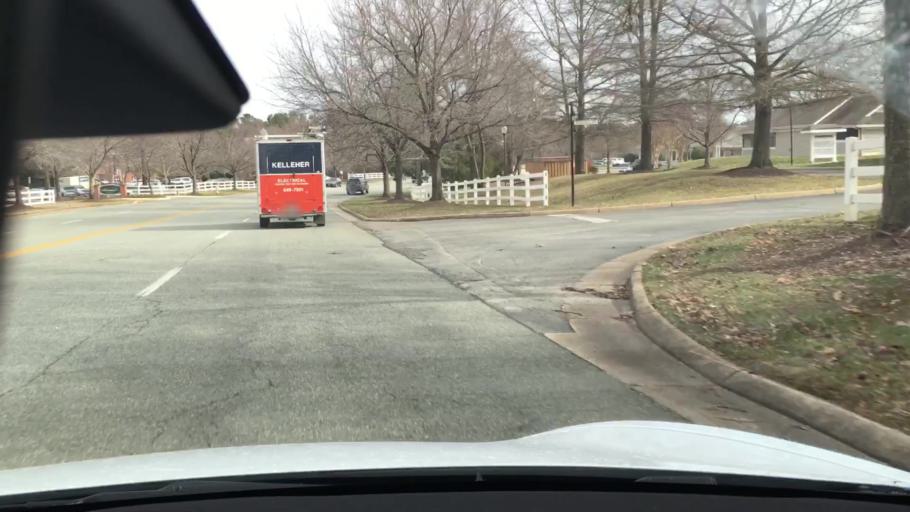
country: US
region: Virginia
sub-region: Chesterfield County
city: Bon Air
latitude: 37.5268
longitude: -77.6124
